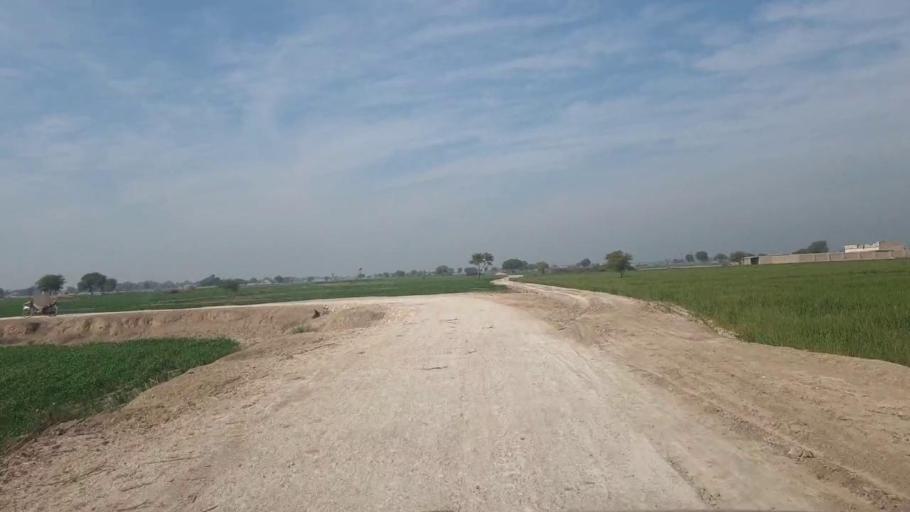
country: PK
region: Sindh
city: Nawabshah
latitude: 26.1632
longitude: 68.5101
